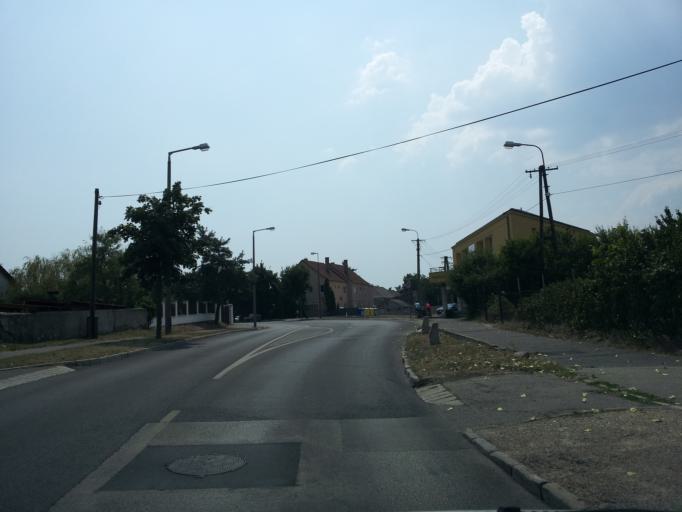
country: HU
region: Veszprem
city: Veszprem
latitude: 47.1005
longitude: 17.9250
